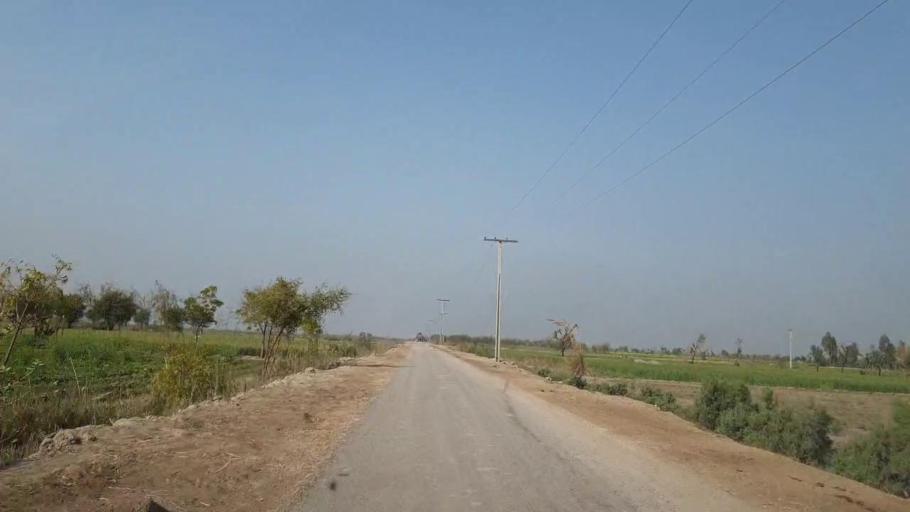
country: PK
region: Sindh
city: Mirpur Khas
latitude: 25.5830
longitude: 69.0406
